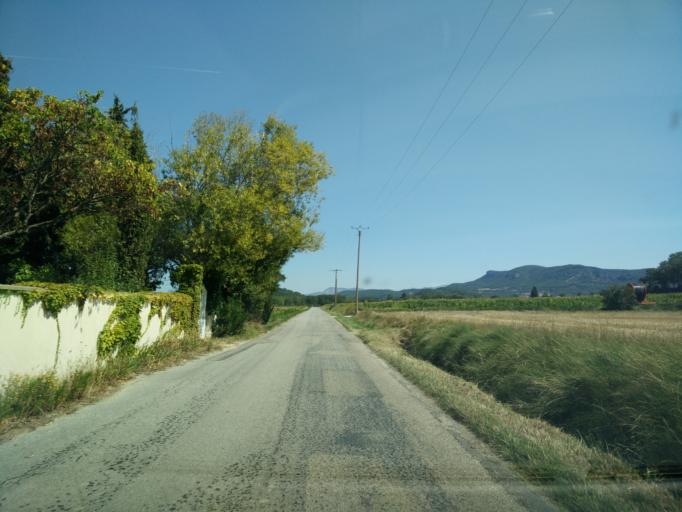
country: FR
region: Rhone-Alpes
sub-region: Departement de la Drome
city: La Begude-de-Mazenc
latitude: 44.5337
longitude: 4.9208
